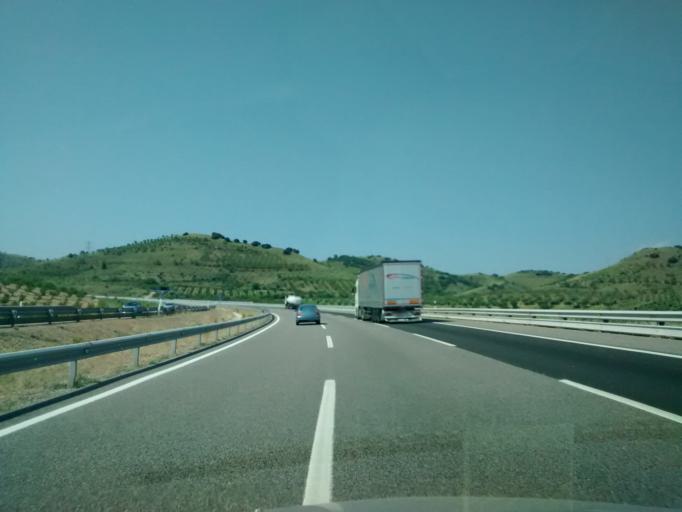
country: ES
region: Aragon
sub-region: Provincia de Zaragoza
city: Morata de Jalon
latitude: 41.4467
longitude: -1.4785
